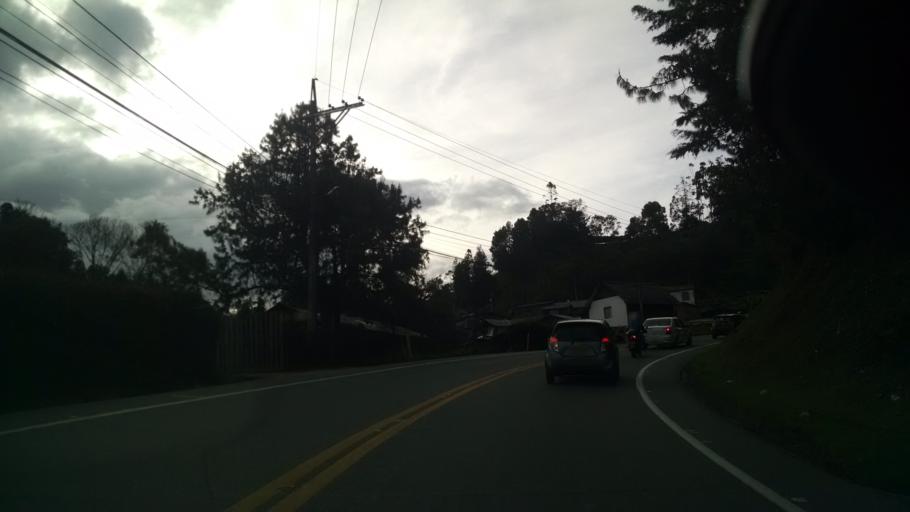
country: CO
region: Antioquia
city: El Retiro
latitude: 6.1394
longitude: -75.5167
